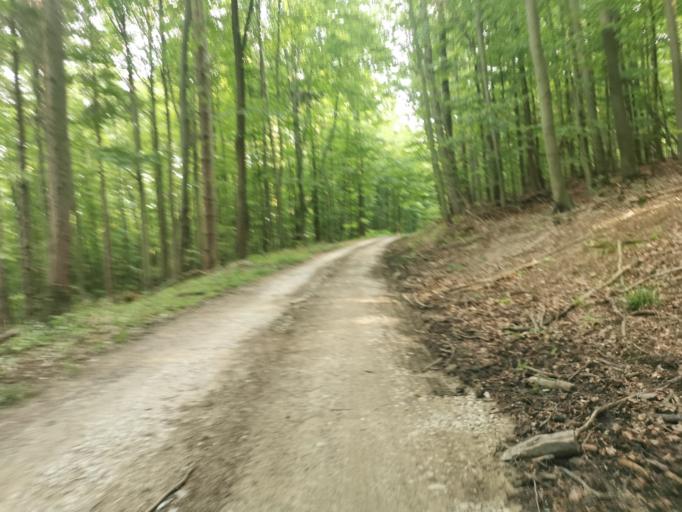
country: SK
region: Trenciansky
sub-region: Okres Myjava
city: Myjava
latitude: 48.8284
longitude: 17.6192
